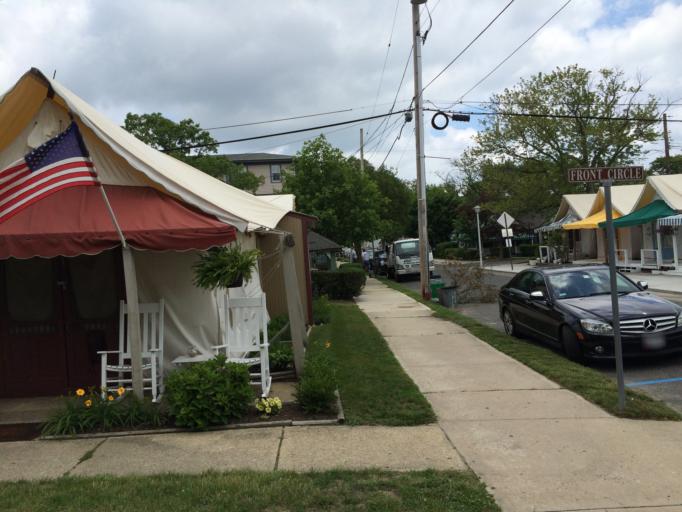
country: US
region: New Jersey
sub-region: Monmouth County
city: Ocean Grove
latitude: 40.2144
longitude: -74.0063
